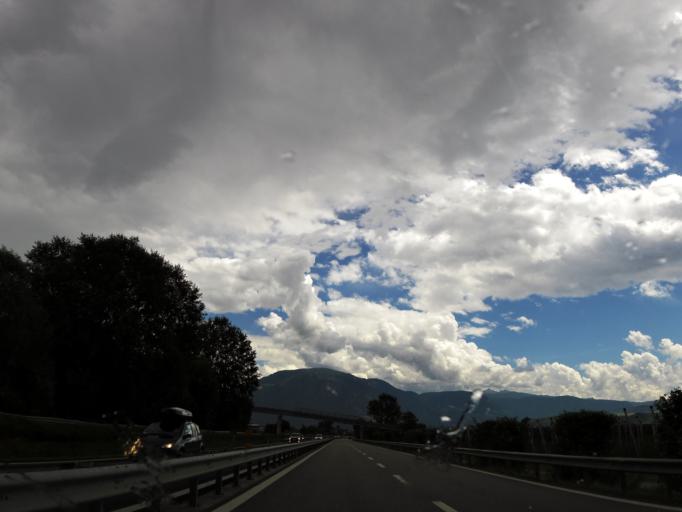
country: IT
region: Trentino-Alto Adige
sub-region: Bolzano
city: Terlano
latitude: 46.5121
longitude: 11.2579
